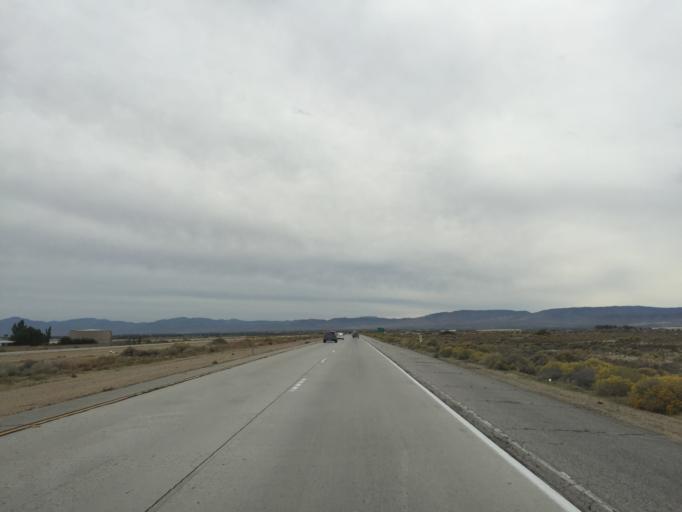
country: US
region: California
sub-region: Los Angeles County
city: Lancaster
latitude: 34.7596
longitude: -118.1708
